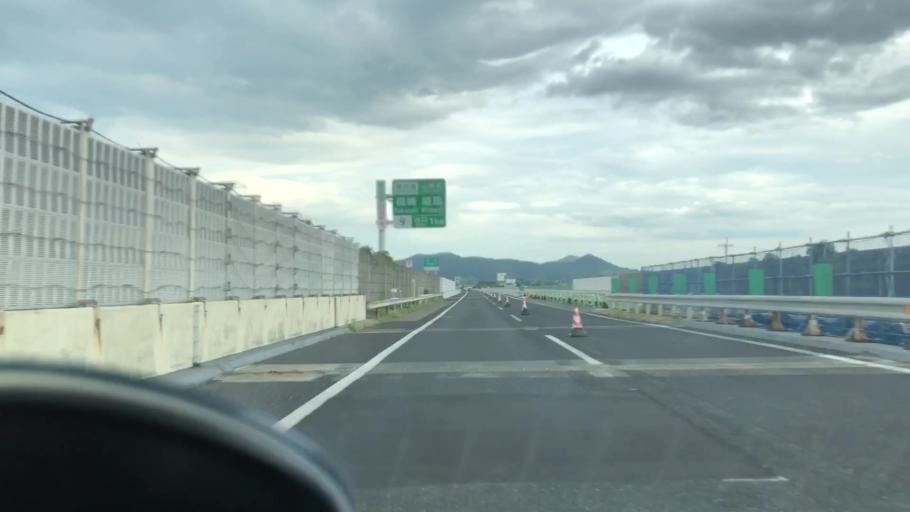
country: JP
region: Hyogo
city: Himeji
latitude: 34.9515
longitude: 134.7506
